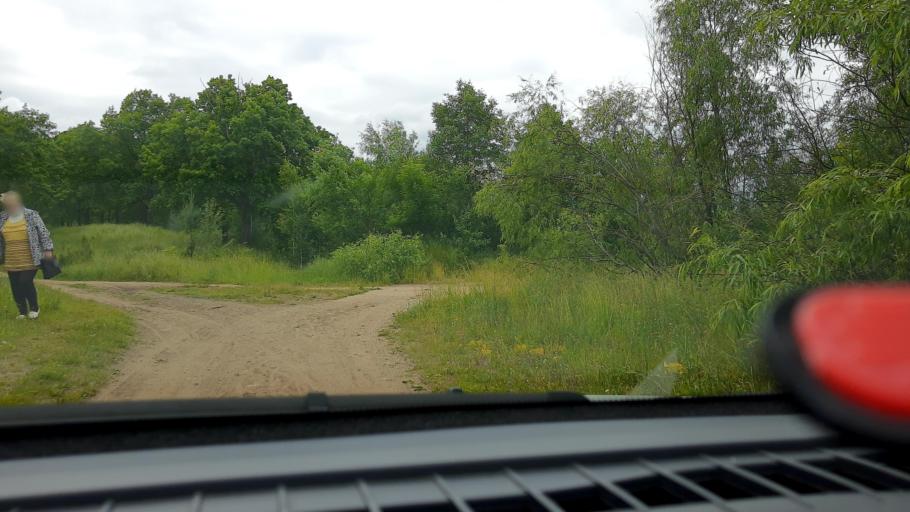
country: RU
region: Nizjnij Novgorod
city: Burevestnik
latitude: 56.2093
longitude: 43.8372
